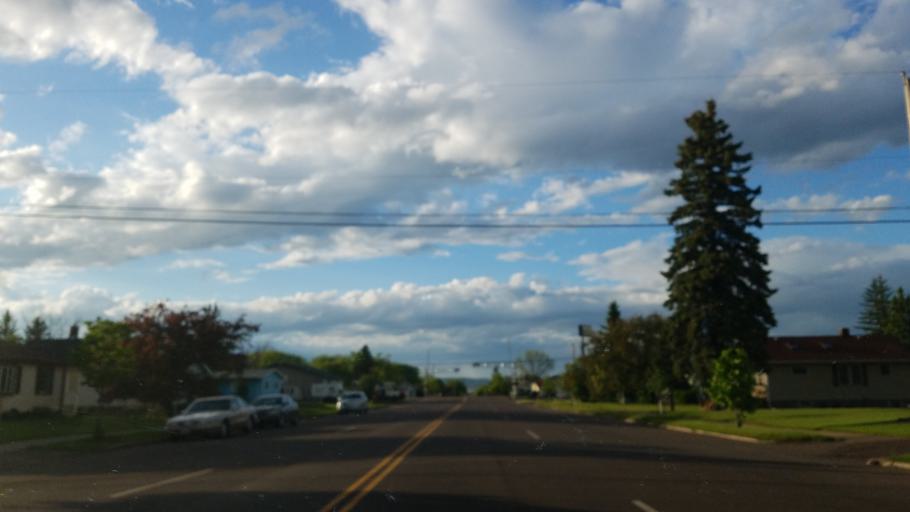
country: US
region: Wisconsin
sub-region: Douglas County
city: Superior
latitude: 46.7267
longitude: -92.0934
